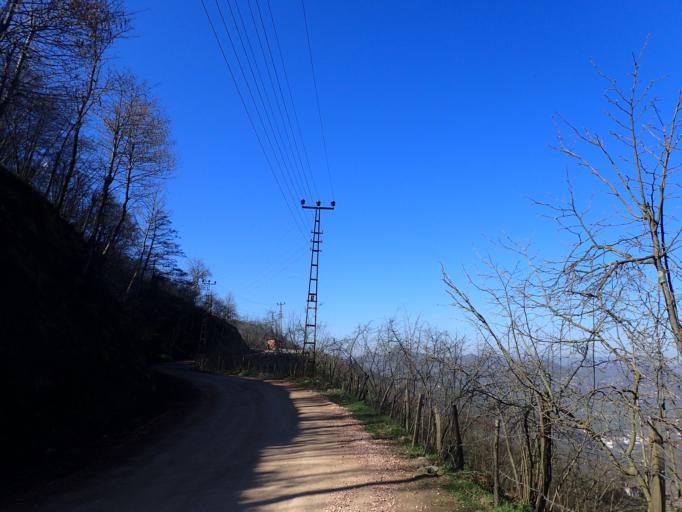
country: TR
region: Ordu
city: Camas
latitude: 40.8703
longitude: 37.4997
